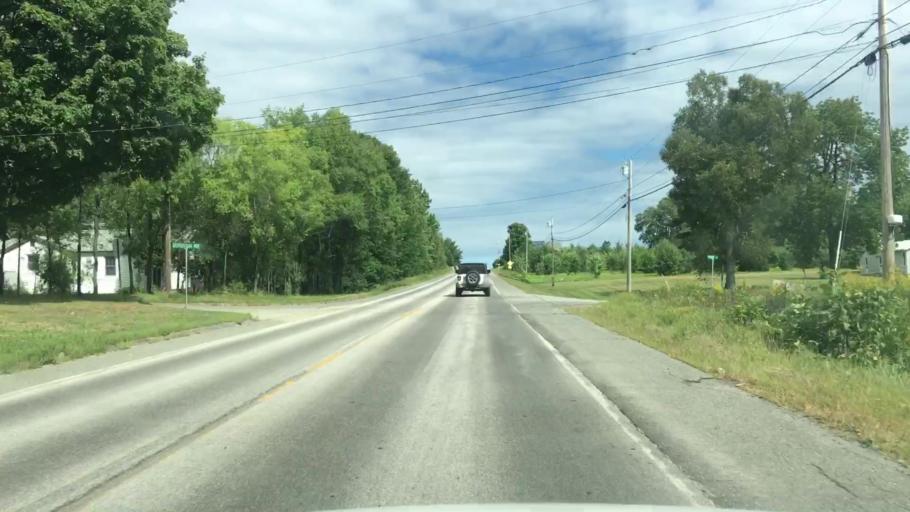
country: US
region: Maine
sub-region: Piscataquis County
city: Dover-Foxcroft
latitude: 45.1604
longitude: -69.2324
